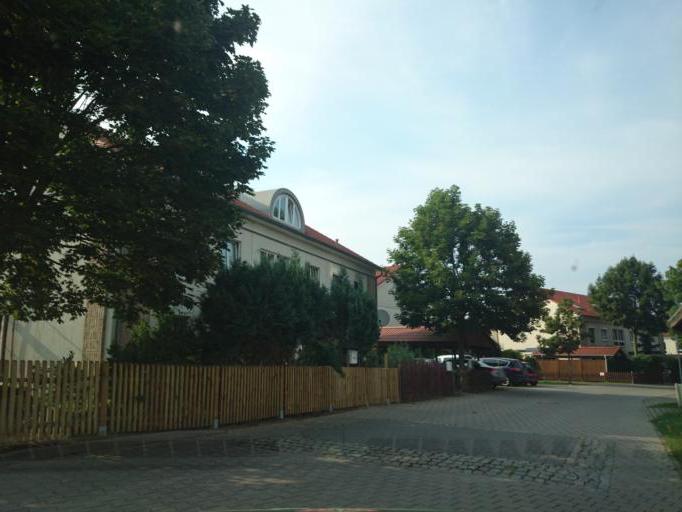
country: DE
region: Berlin
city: Lichtenrade
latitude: 52.3701
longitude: 13.3950
